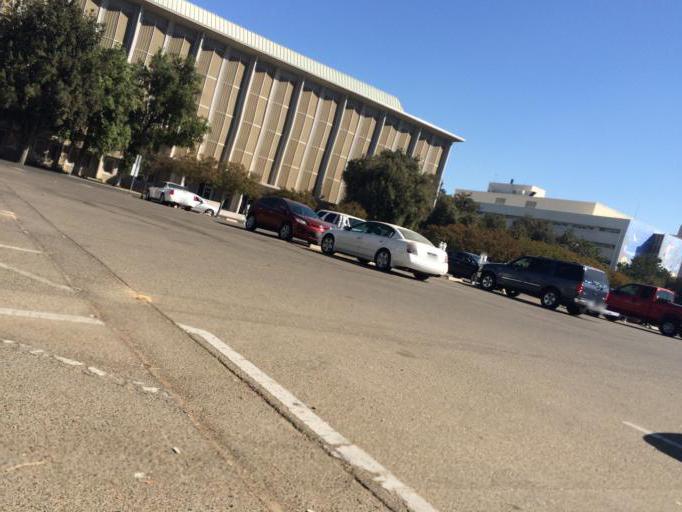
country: US
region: California
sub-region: Fresno County
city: Fresno
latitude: 36.7389
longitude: -119.7872
